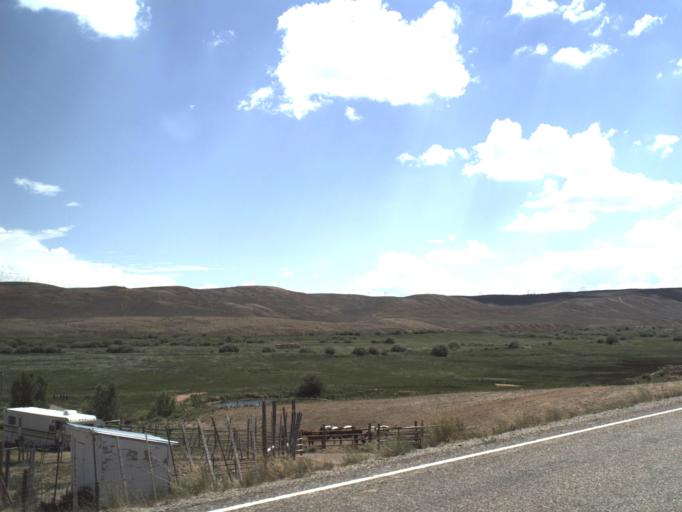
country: US
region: Utah
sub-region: Rich County
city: Randolph
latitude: 41.5170
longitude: -111.2102
